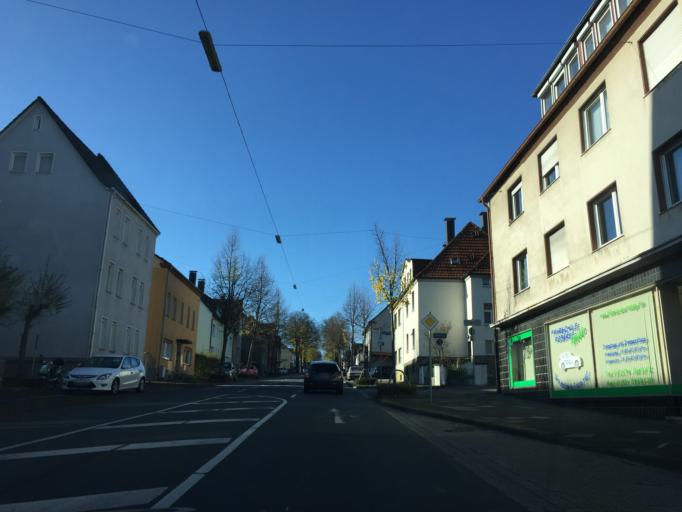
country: DE
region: North Rhine-Westphalia
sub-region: Regierungsbezirk Arnsberg
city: Nachrodt-Wiblingwerde
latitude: 51.3648
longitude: 7.6018
